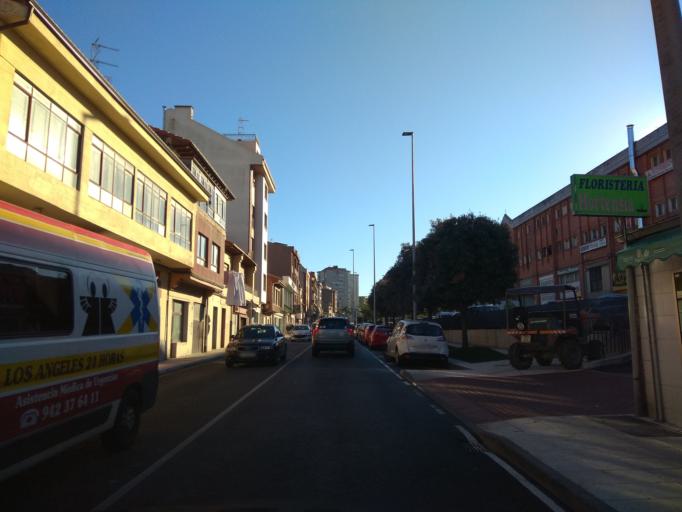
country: ES
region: Cantabria
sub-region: Provincia de Cantabria
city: Santander
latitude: 43.4628
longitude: -3.8384
